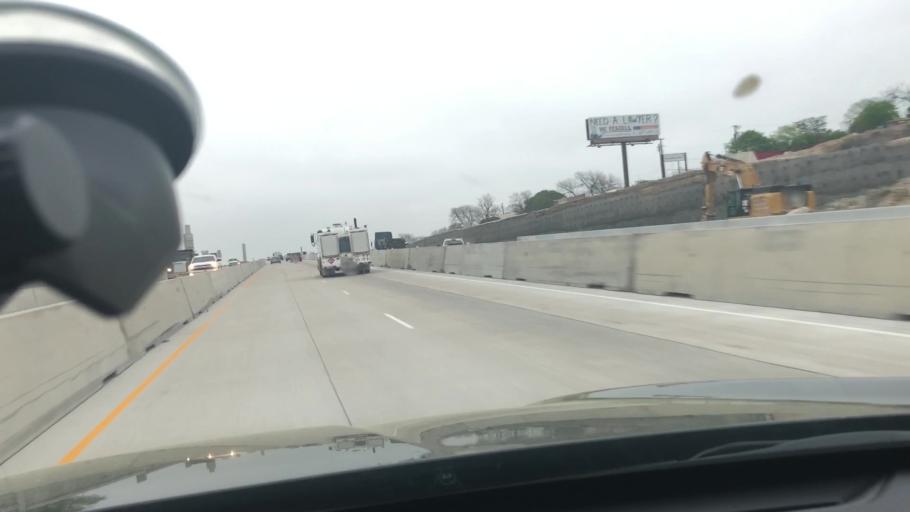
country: US
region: Texas
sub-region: Bell County
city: Temple
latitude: 31.0951
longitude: -97.3731
